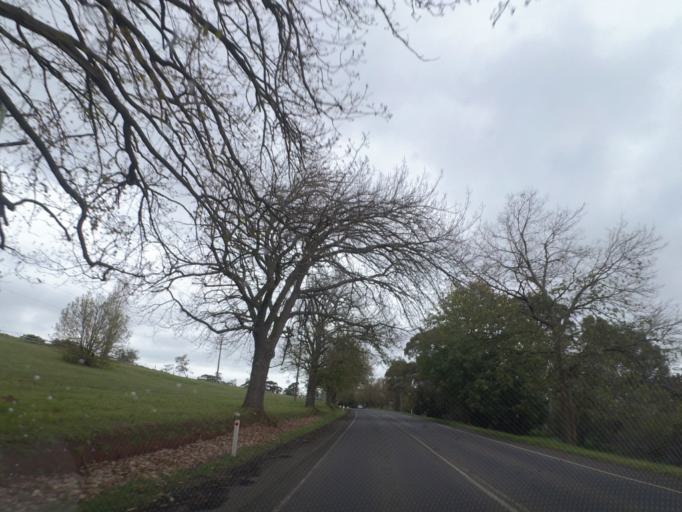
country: AU
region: Victoria
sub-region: Hume
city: Sunbury
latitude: -37.3432
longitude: 144.5316
